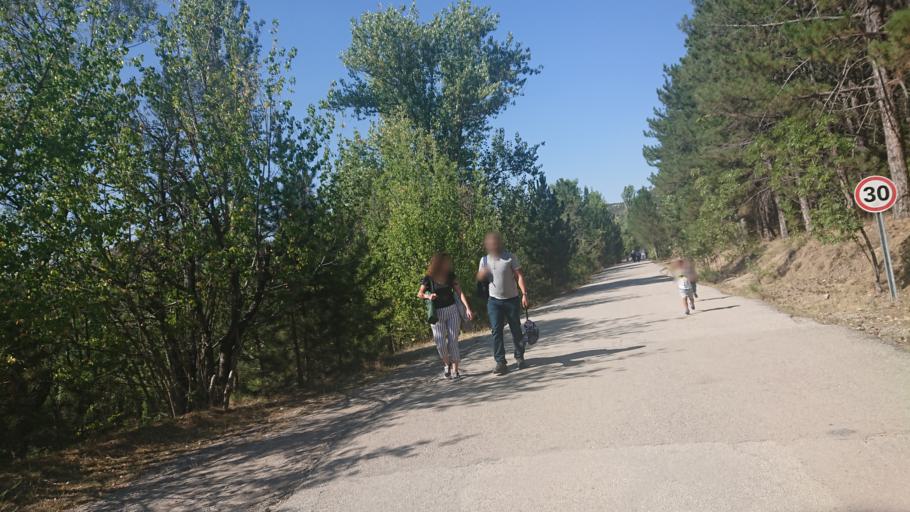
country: TR
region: Ankara
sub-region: Goelbasi
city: Golbasi
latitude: 39.8161
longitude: 32.8211
